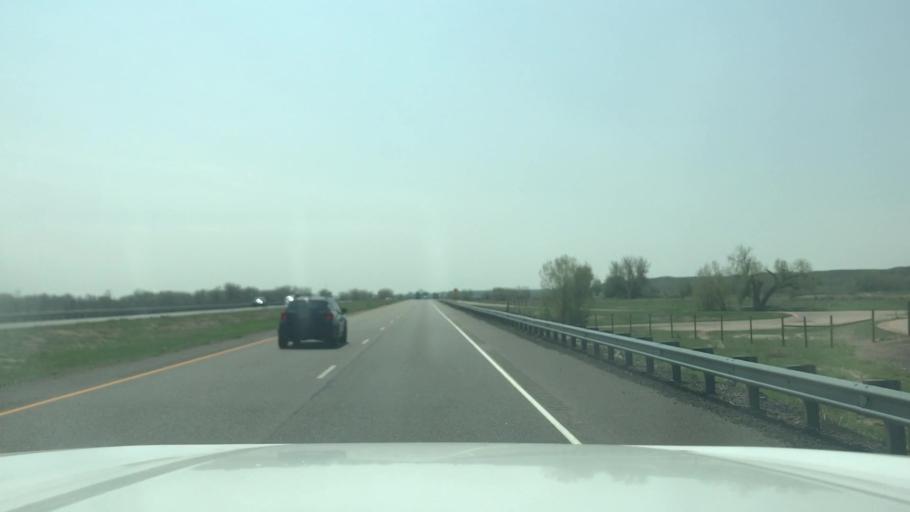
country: US
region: Colorado
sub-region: El Paso County
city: Fountain
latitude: 38.6292
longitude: -104.6910
